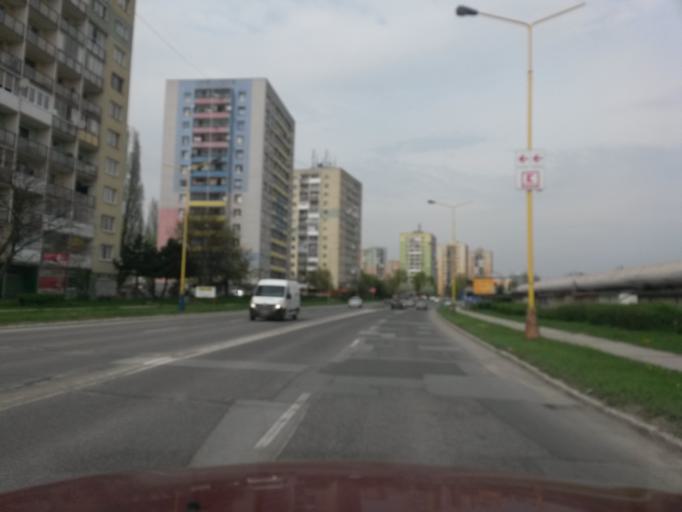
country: SK
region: Kosicky
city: Kosice
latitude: 48.7105
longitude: 21.2652
